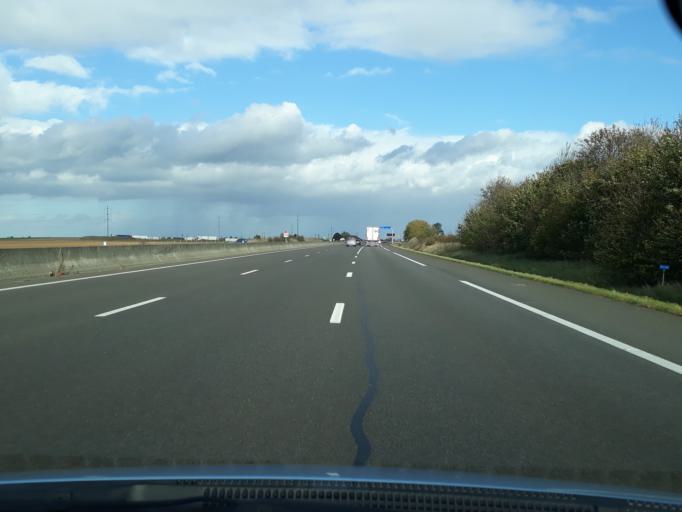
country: FR
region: Centre
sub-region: Departement du Loiret
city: Beaugency
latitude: 47.8159
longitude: 1.6338
